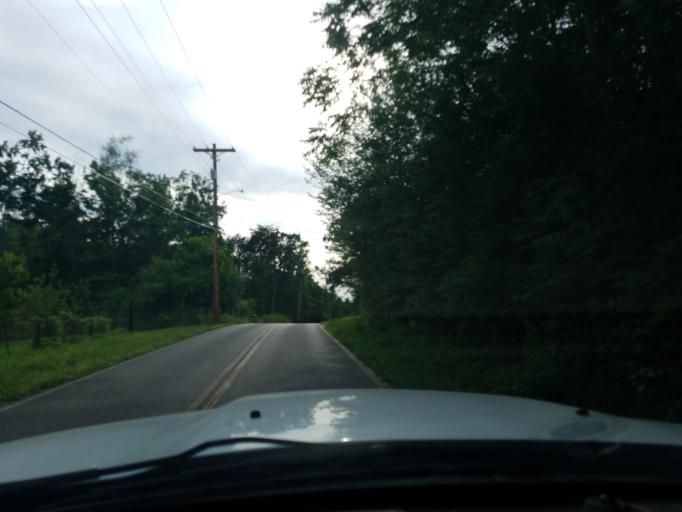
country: US
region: Tennessee
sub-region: Putnam County
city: Cookeville
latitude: 36.1288
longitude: -85.5602
